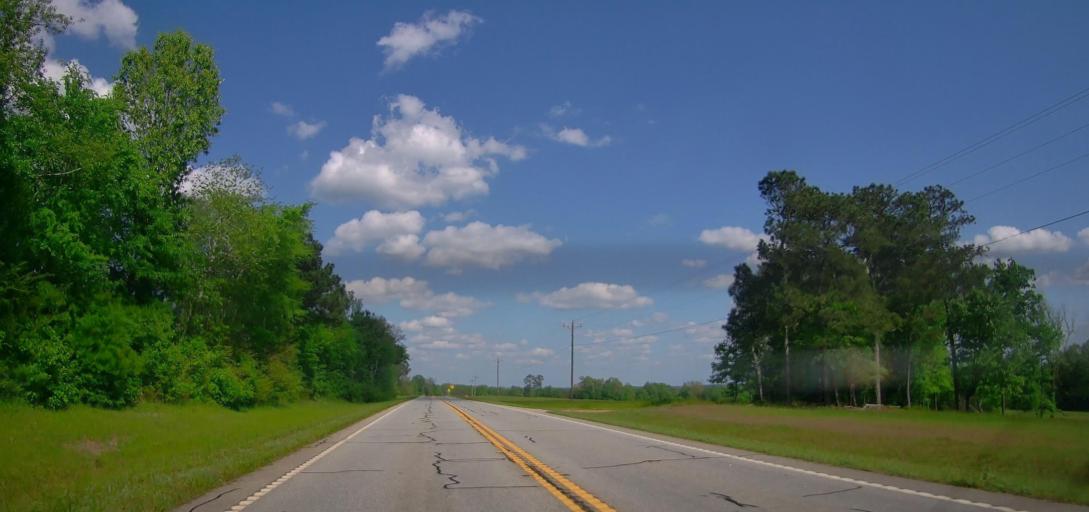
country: US
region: Georgia
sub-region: Greene County
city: Greensboro
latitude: 33.5965
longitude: -83.2973
